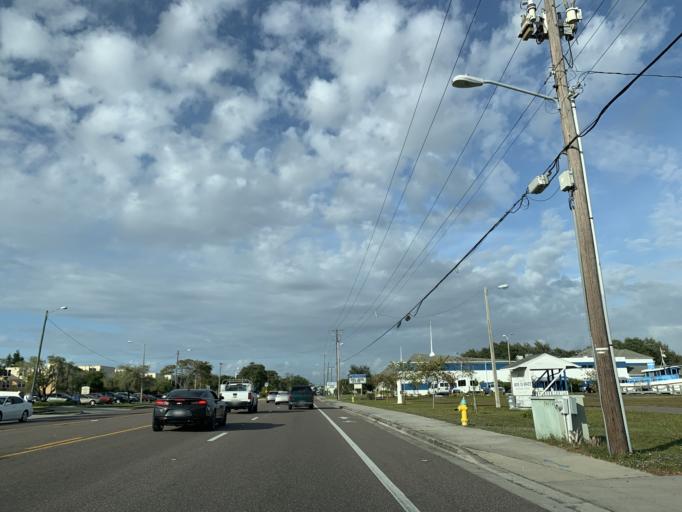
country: US
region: Florida
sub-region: Hillsborough County
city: Tampa
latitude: 27.9038
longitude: -82.5184
